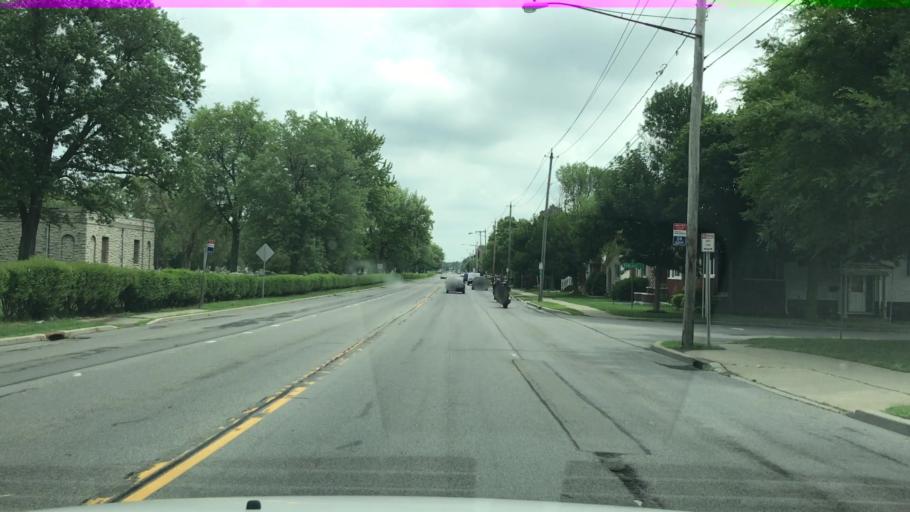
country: US
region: New York
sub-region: Erie County
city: Sloan
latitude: 42.9202
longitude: -78.7920
